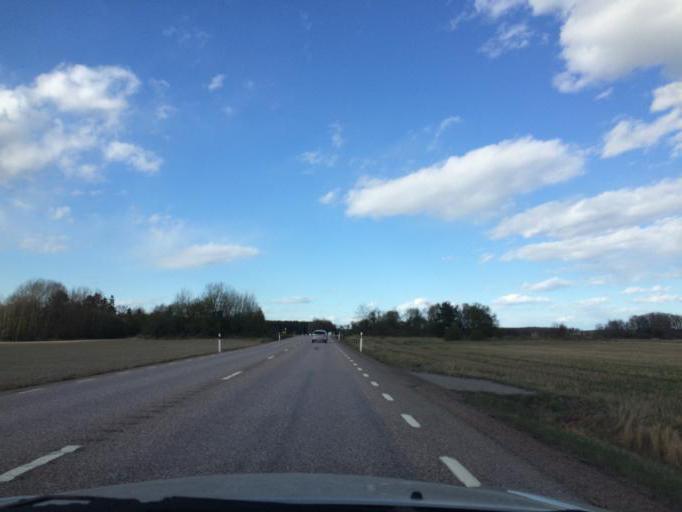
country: SE
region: Vaestmanland
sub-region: Hallstahammars Kommun
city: Kolback
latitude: 59.5421
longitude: 16.3275
